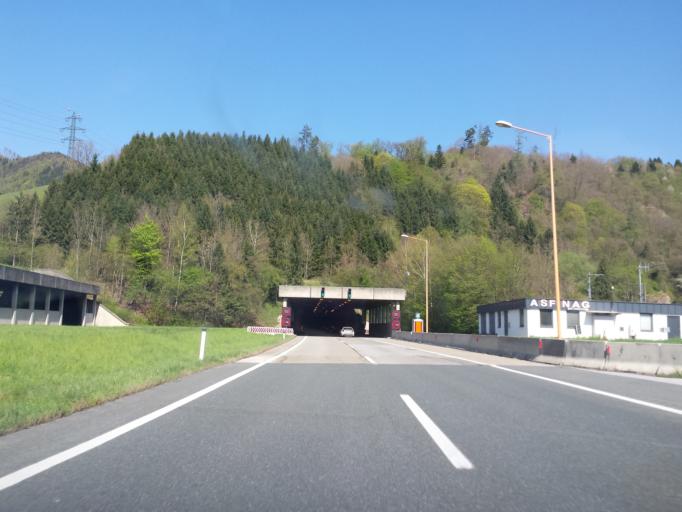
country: AT
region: Styria
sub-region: Politischer Bezirk Graz-Umgebung
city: Deutschfeistritz
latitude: 47.1906
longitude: 15.3295
